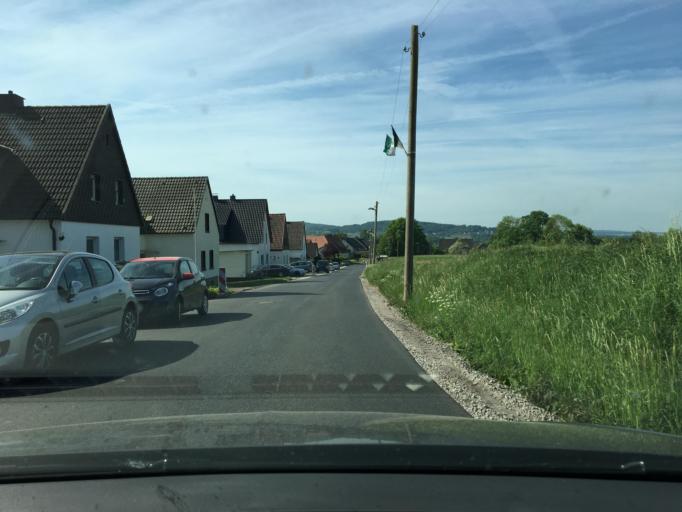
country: DE
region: North Rhine-Westphalia
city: Wickede
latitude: 51.4896
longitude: 7.8265
